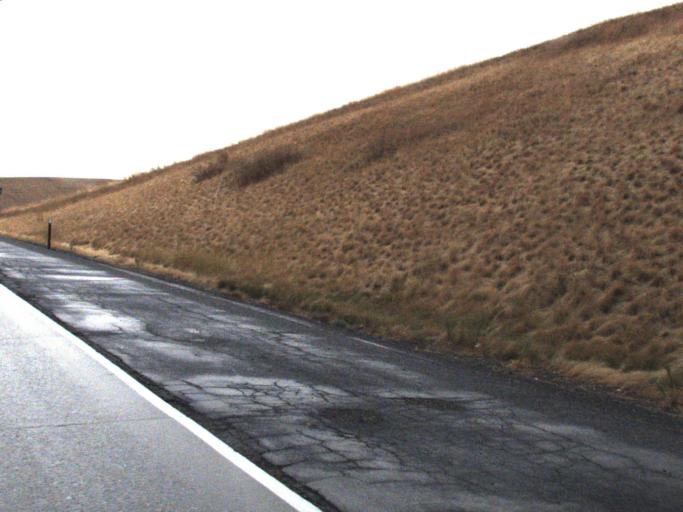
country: US
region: Washington
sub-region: Whitman County
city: Colfax
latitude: 47.1757
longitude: -117.3796
